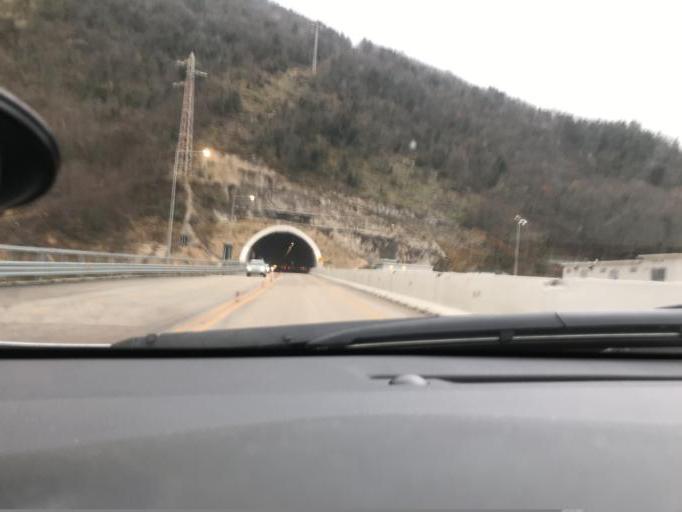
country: IT
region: The Marches
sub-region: Provincia di Ancona
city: Serra San Quirico
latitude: 43.4304
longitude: 13.0115
